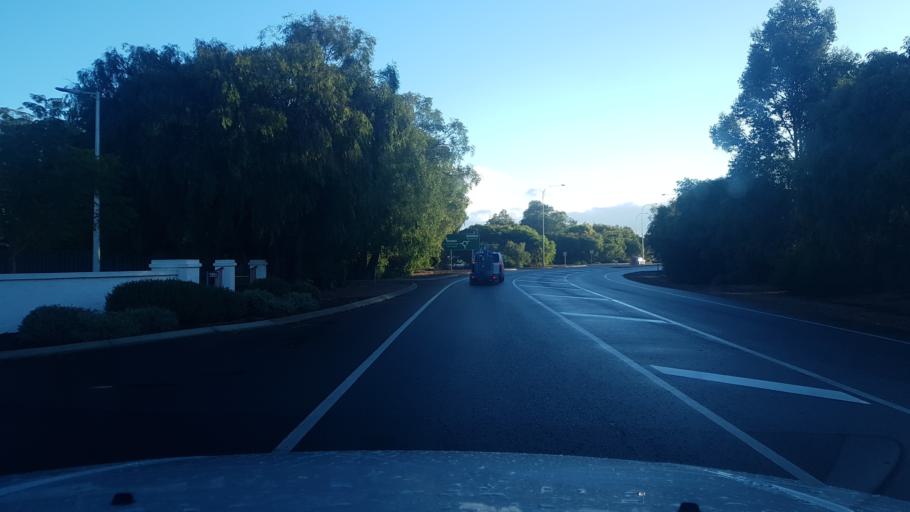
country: AU
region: Western Australia
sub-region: Busselton
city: Vasse
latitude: -33.6631
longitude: 115.2586
